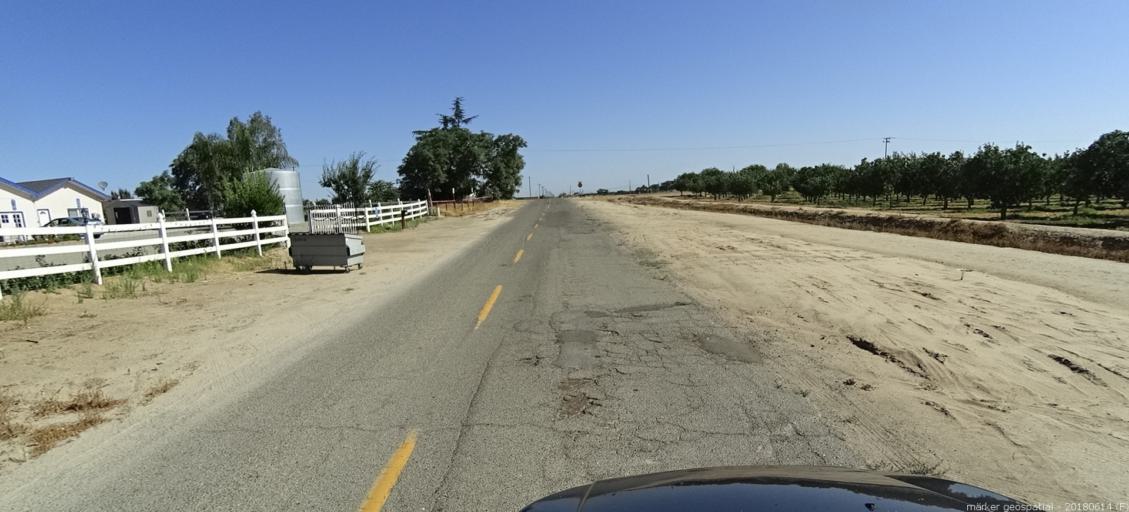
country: US
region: California
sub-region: Madera County
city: Fairmead
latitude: 37.0171
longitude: -120.1661
